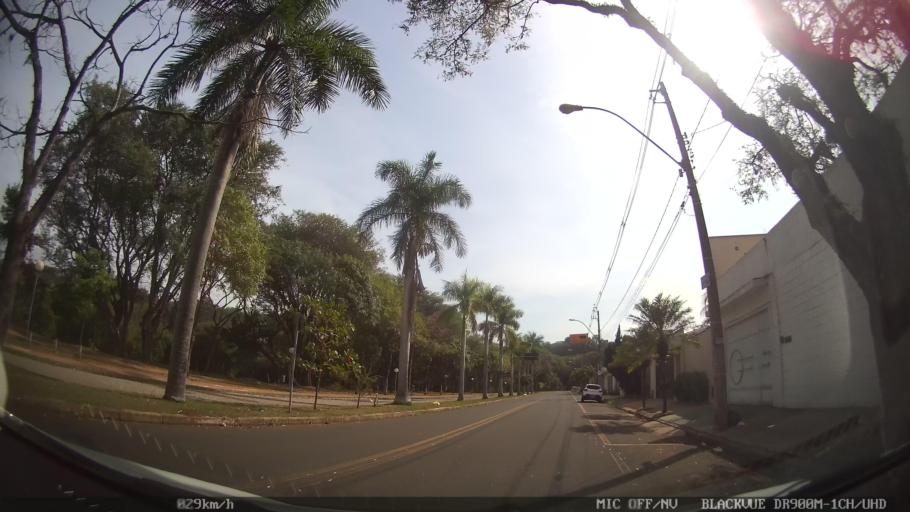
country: BR
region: Sao Paulo
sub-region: Piracicaba
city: Piracicaba
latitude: -22.7182
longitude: -47.6749
